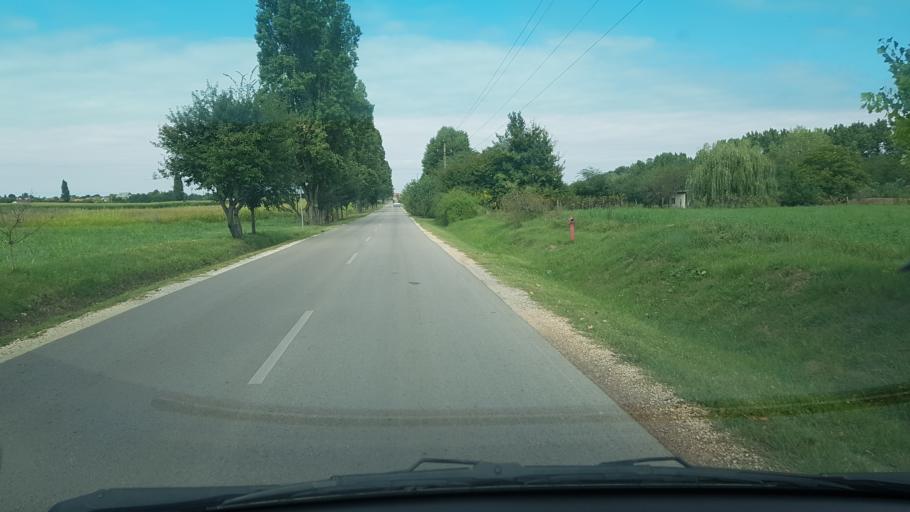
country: HU
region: Pest
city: Dunavarsany
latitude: 47.2840
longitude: 19.0465
